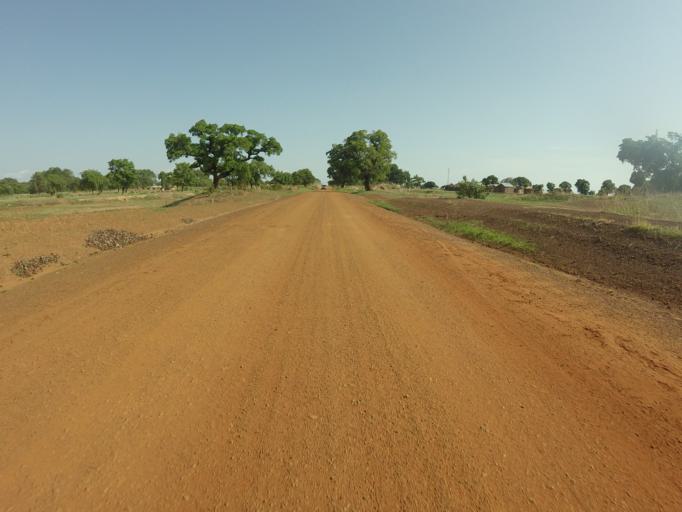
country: GH
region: Upper East
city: Bawku
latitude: 10.7703
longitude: -0.1948
